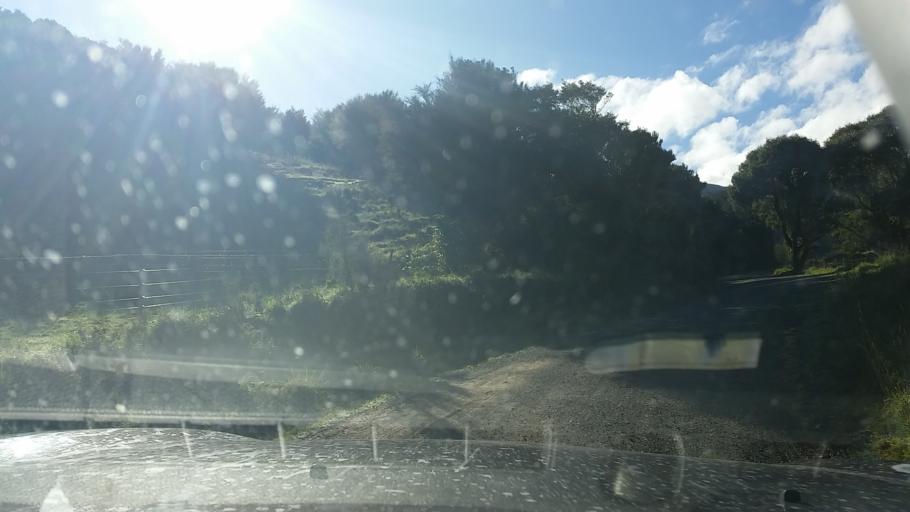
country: NZ
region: Marlborough
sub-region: Marlborough District
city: Picton
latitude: -41.1466
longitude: 174.0501
